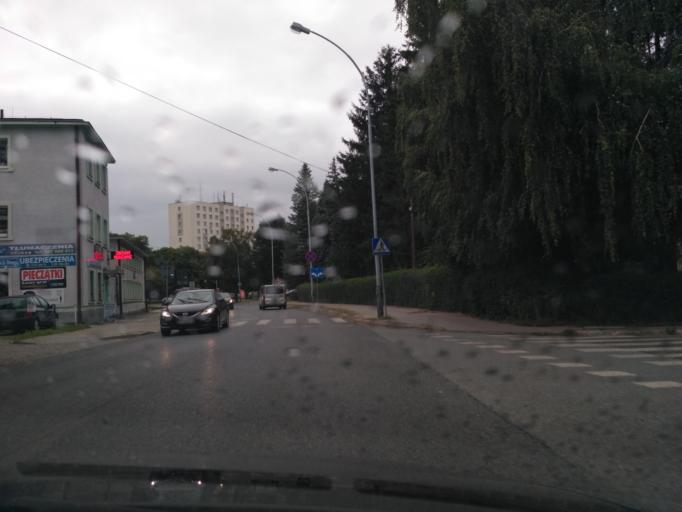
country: PL
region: Subcarpathian Voivodeship
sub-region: Krosno
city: Krosno
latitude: 49.6828
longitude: 21.7734
